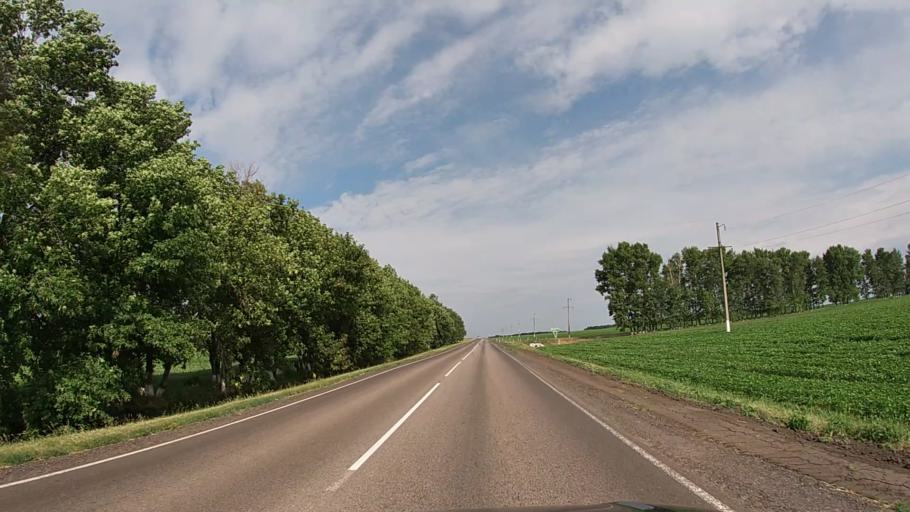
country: RU
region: Belgorod
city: Krasnaya Yaruga
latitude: 50.8055
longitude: 35.5476
